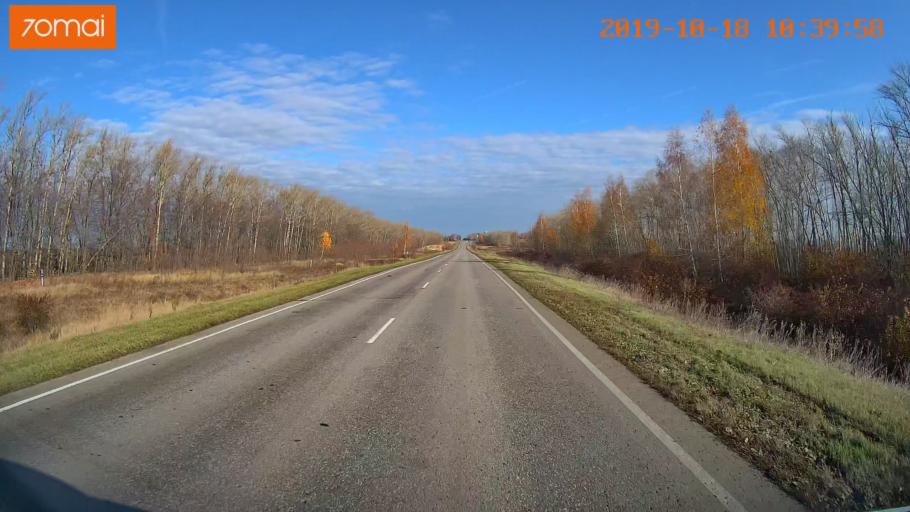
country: RU
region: Tula
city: Kurkino
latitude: 53.5945
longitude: 38.6586
